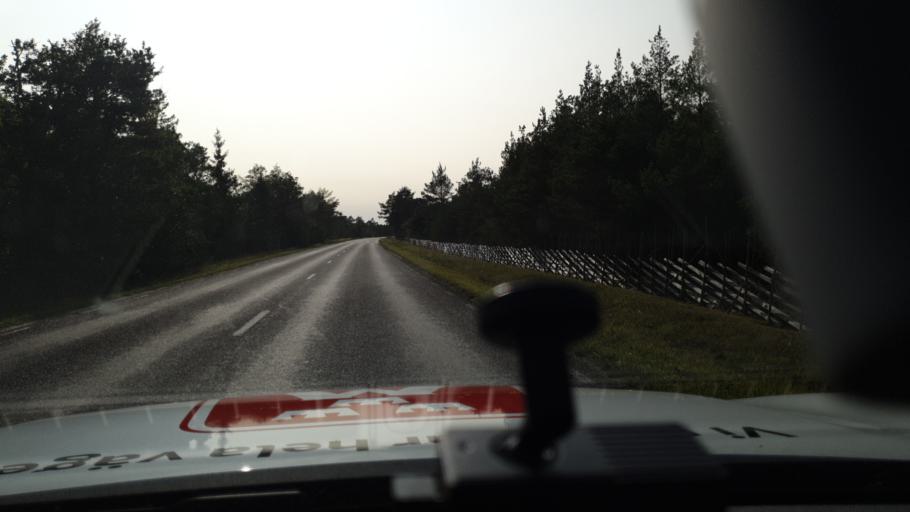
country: SE
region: Gotland
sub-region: Gotland
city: Slite
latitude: 57.6657
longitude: 18.6982
